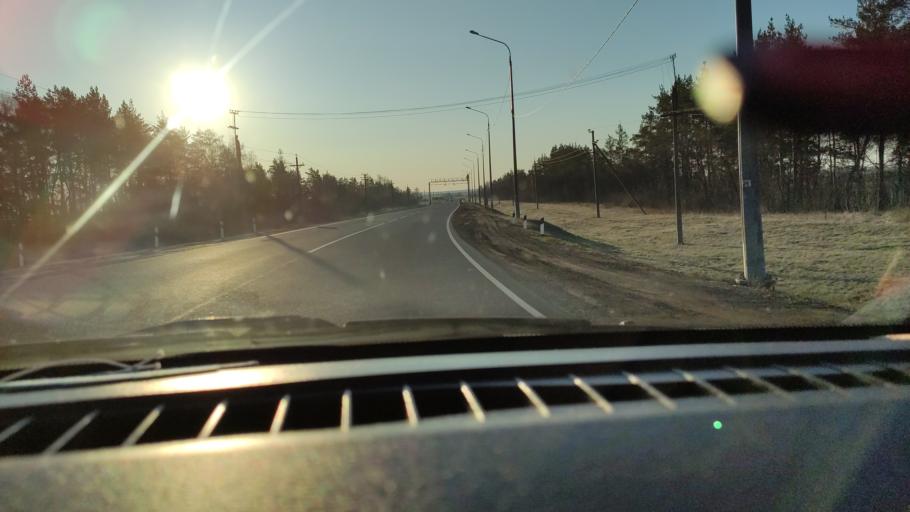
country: RU
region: Saratov
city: Sennoy
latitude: 52.1522
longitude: 46.9662
